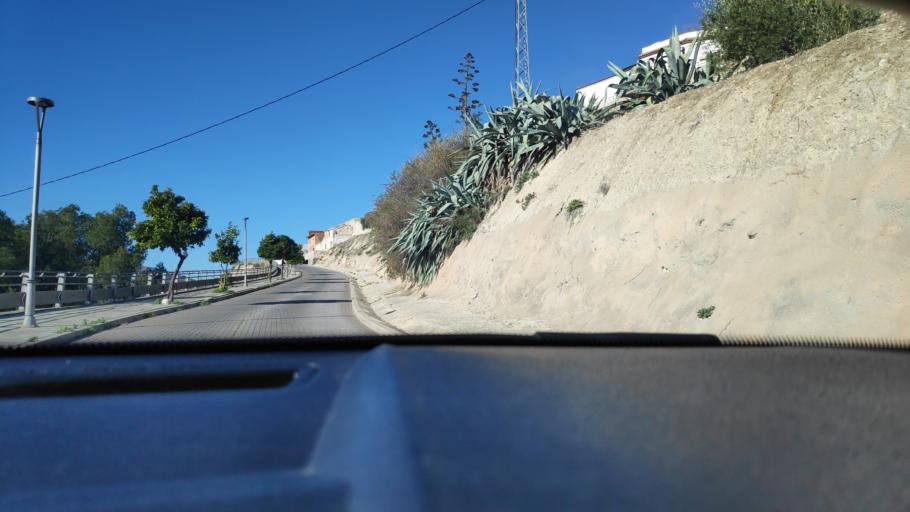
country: ES
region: Andalusia
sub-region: Province of Cordoba
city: Baena
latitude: 37.6116
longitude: -4.3302
